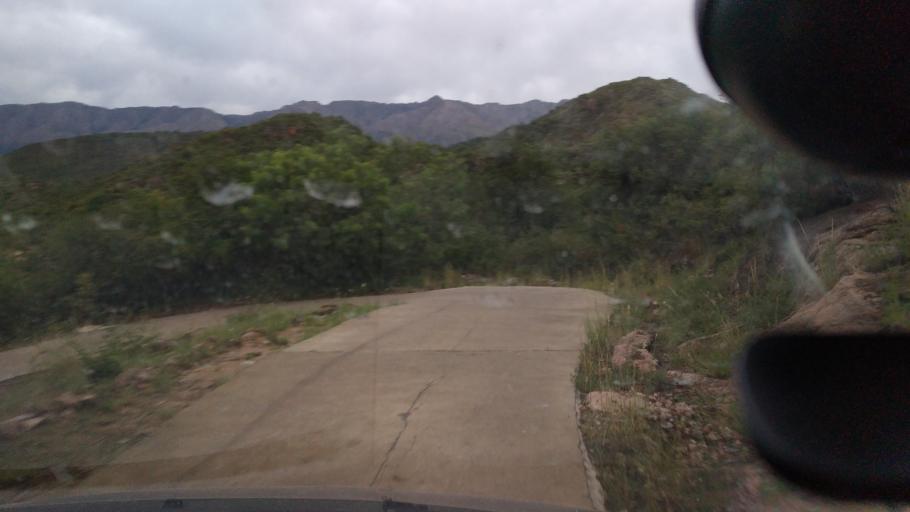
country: AR
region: Cordoba
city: Villa Las Rosas
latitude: -31.8782
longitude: -65.0226
